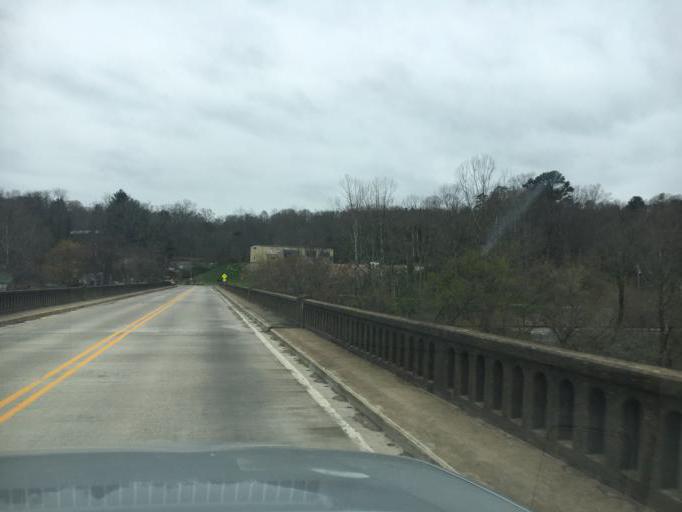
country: US
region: North Carolina
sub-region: Buncombe County
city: Woodfin
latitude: 35.6285
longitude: -82.6017
